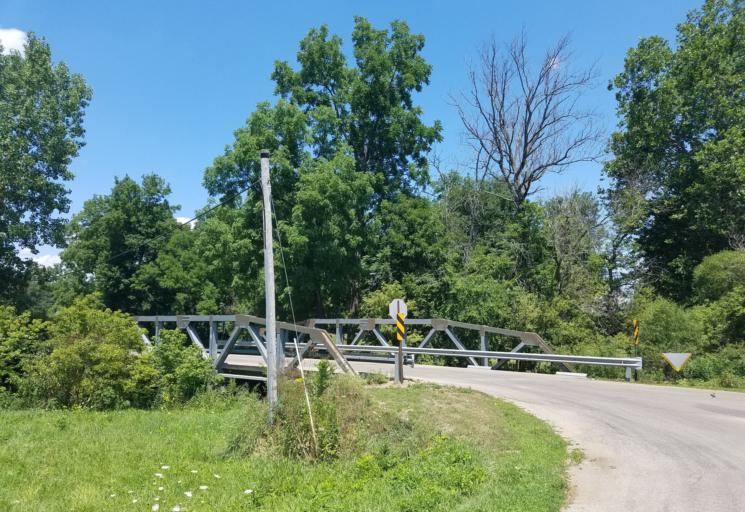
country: US
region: Ohio
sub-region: Knox County
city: Fredericktown
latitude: 40.4603
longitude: -82.6299
